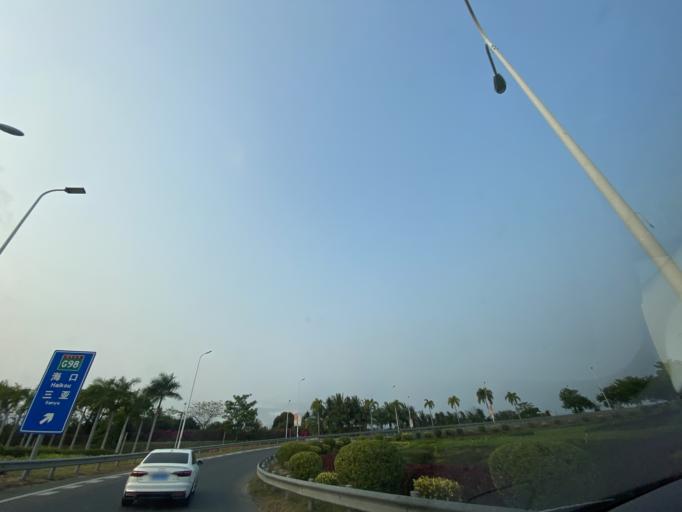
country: CN
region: Hainan
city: Haitangwan
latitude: 18.3905
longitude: 109.7304
